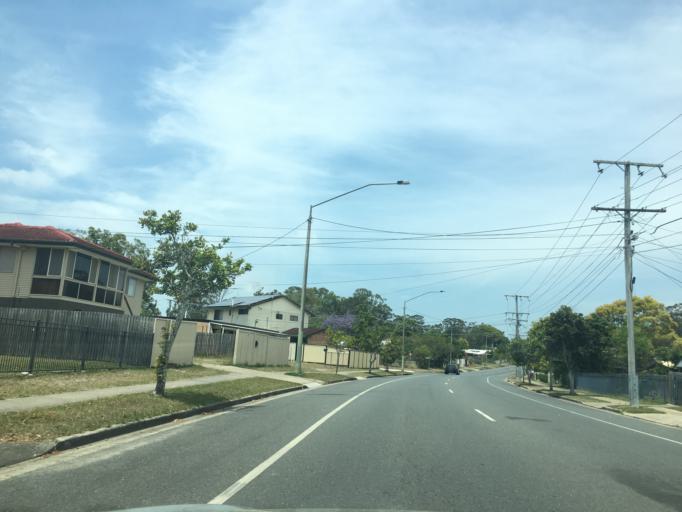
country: AU
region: Queensland
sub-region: Logan
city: Logan City
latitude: -27.6567
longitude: 153.1015
